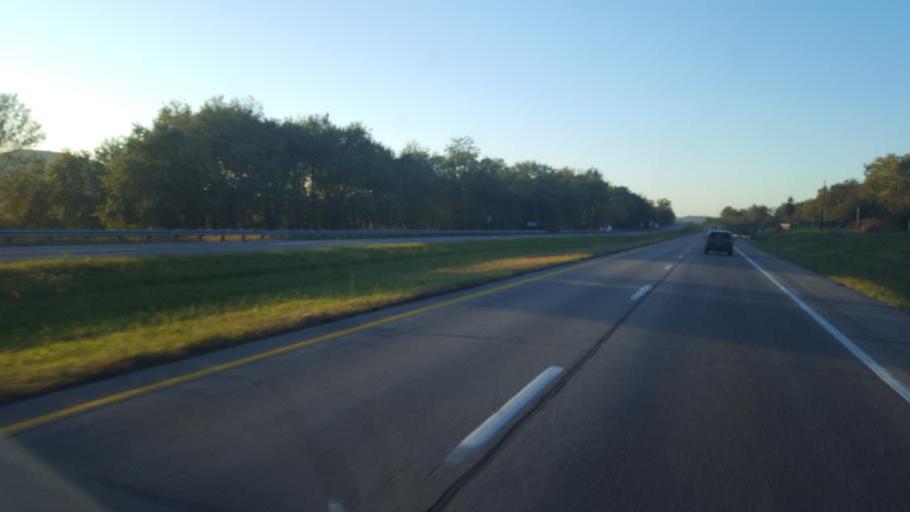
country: US
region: Ohio
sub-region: Scioto County
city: Lucasville
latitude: 38.9106
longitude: -83.0109
